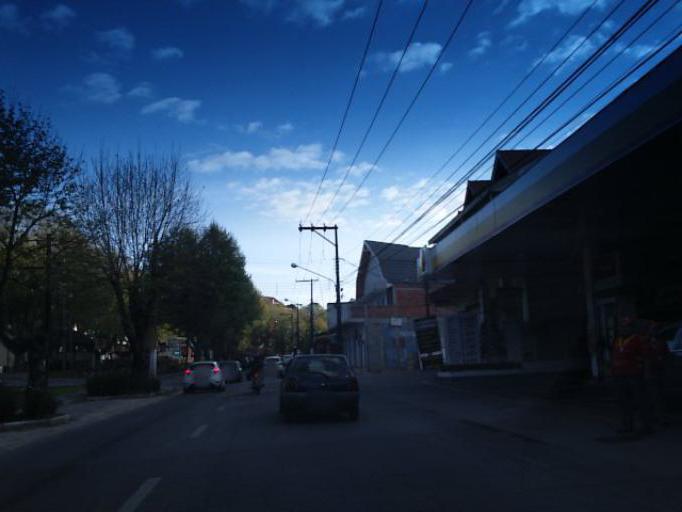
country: BR
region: Sao Paulo
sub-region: Campos Do Jordao
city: Campos do Jordao
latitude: -22.7344
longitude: -45.5865
